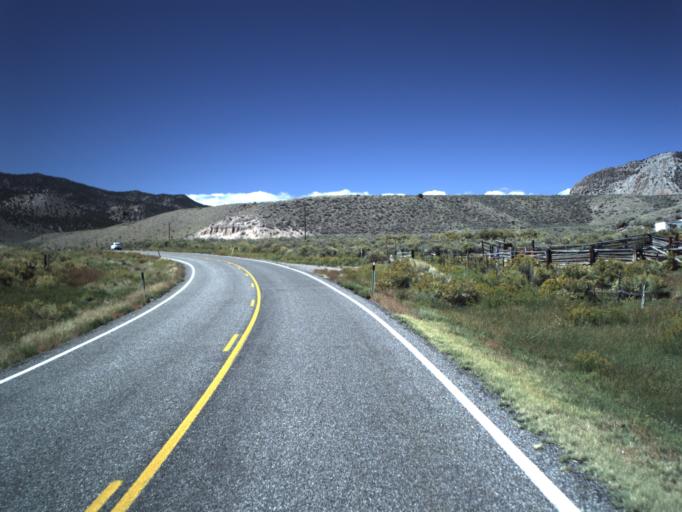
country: US
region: Utah
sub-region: Piute County
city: Junction
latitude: 38.1690
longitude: -112.0433
